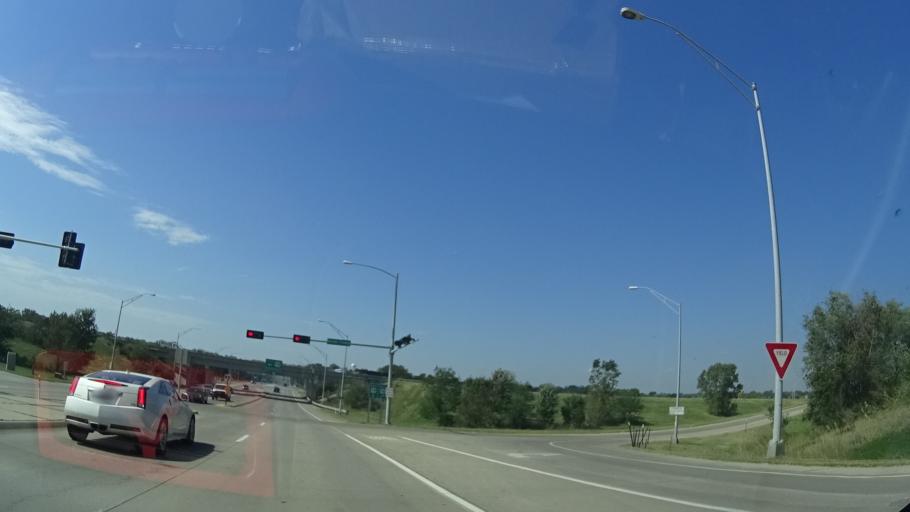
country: US
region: Nebraska
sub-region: Sarpy County
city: Offutt Air Force Base
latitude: 41.1177
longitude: -95.9330
